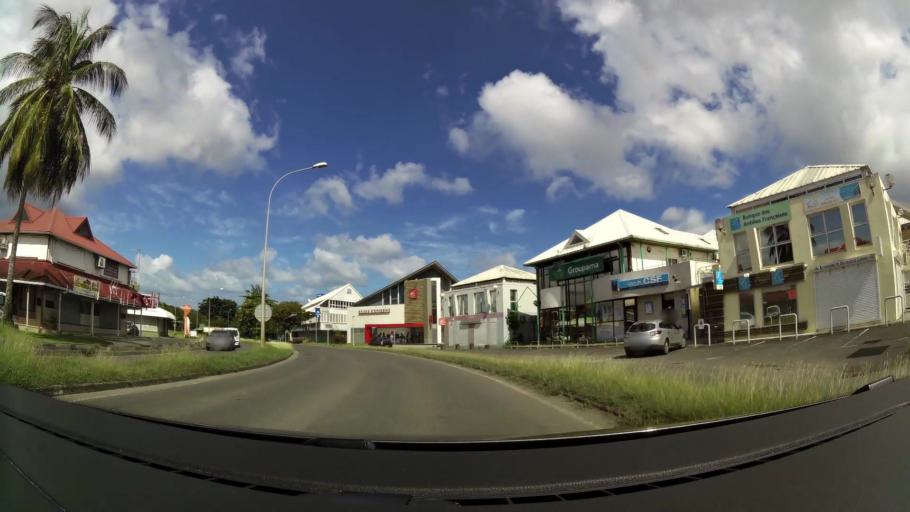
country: GP
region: Guadeloupe
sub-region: Guadeloupe
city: Pointe-a-Pitre
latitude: 16.2507
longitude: -61.5322
